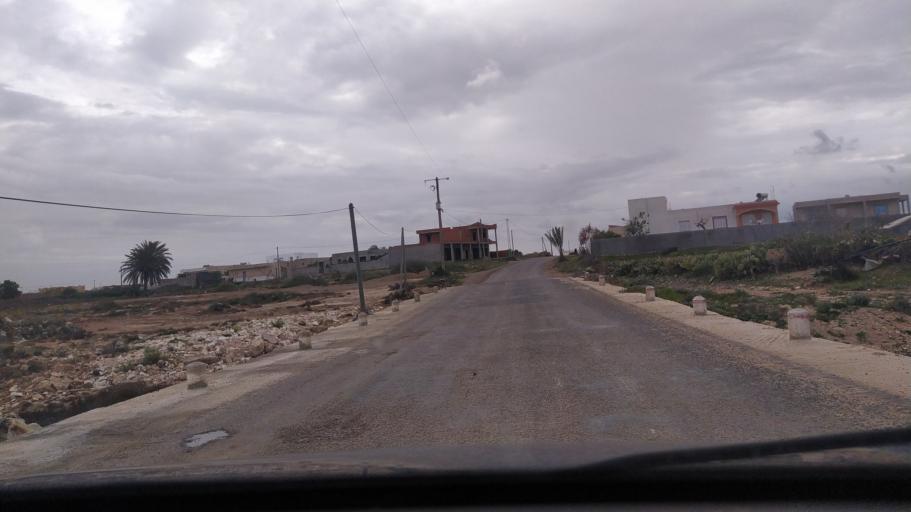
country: TN
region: Al Munastir
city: Sidi Bin Nur
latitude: 35.5108
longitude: 10.9643
